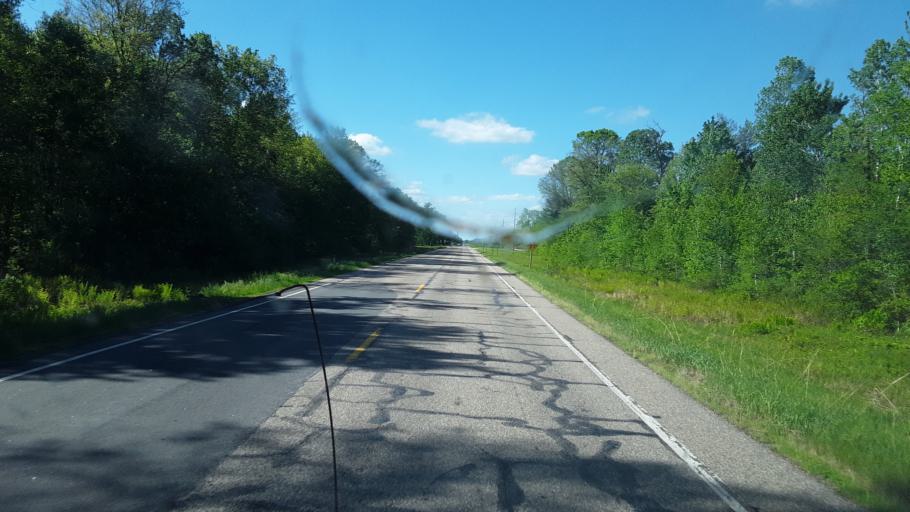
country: US
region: Wisconsin
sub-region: Wood County
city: Nekoosa
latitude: 44.2104
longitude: -90.1367
